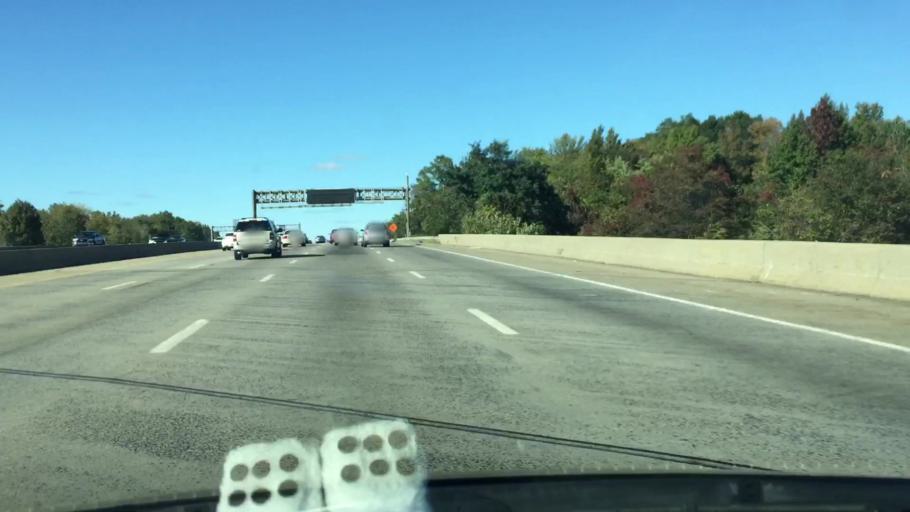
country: US
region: New Jersey
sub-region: Camden County
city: Bellmawr
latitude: 39.8530
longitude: -75.0971
